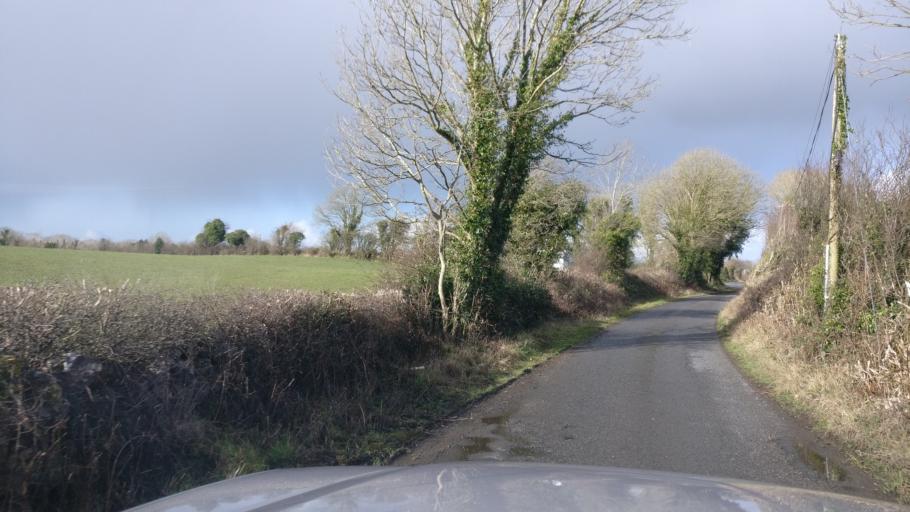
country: IE
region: Connaught
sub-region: County Galway
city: Oranmore
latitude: 53.2361
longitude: -8.8292
